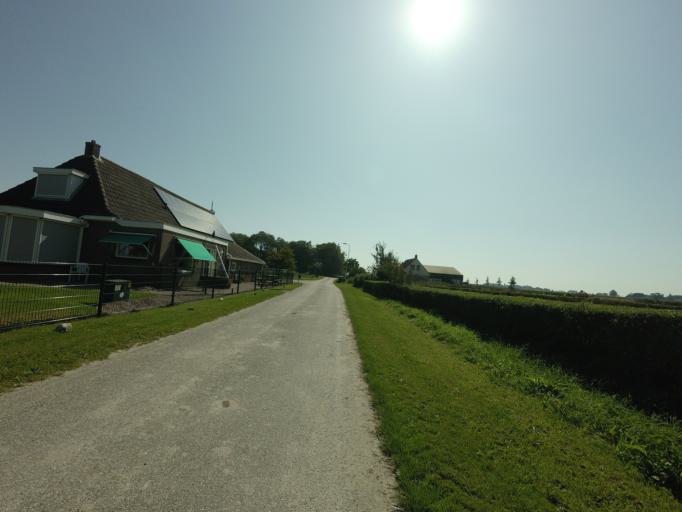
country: NL
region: Friesland
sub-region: Gemeente Dongeradeel
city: Holwerd
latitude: 53.3673
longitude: 5.9233
